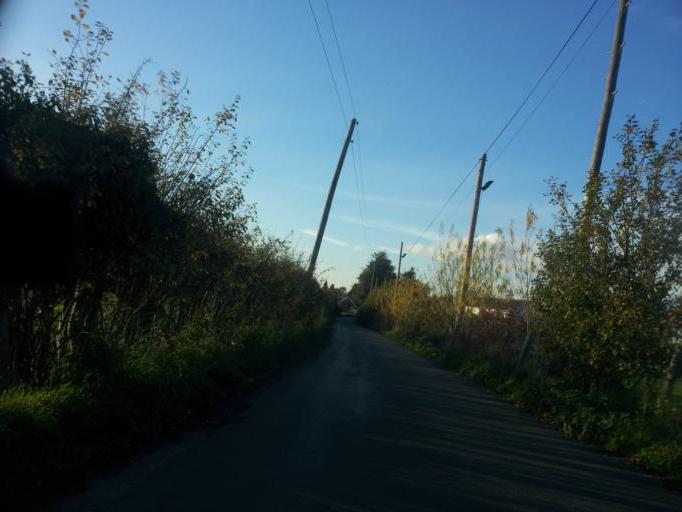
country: GB
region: England
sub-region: Kent
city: Newington
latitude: 51.3737
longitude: 0.6556
